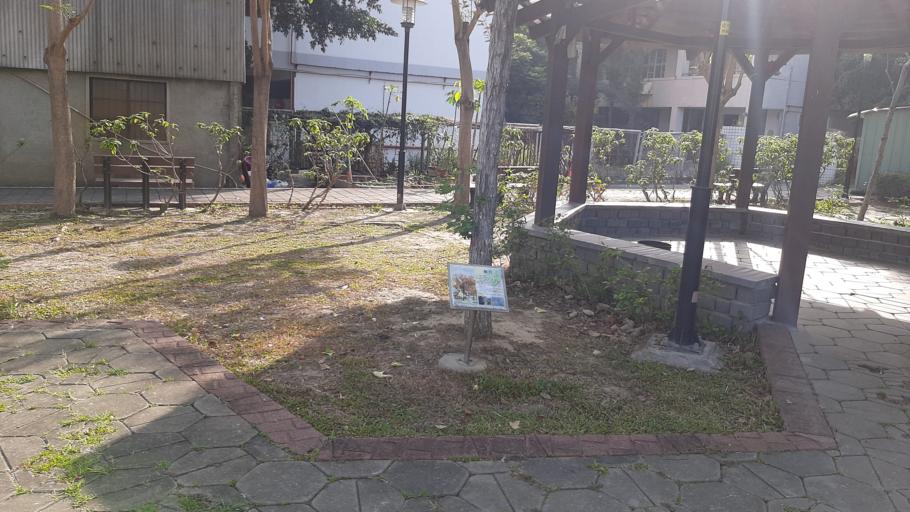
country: TW
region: Taiwan
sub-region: Taichung City
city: Taichung
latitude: 24.1247
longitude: 120.7252
